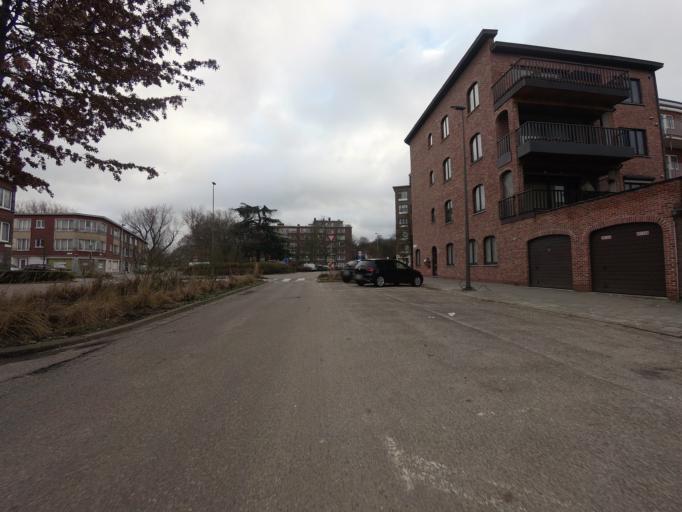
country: BE
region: Flanders
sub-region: Provincie Antwerpen
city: Hoboken
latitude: 51.1802
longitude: 4.3850
